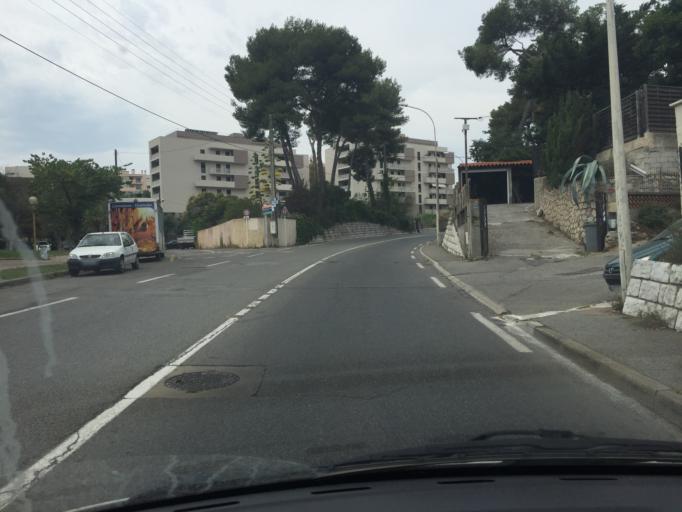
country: FR
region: Provence-Alpes-Cote d'Azur
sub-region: Departement des Alpes-Maritimes
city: Biot
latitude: 43.5940
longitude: 7.0959
